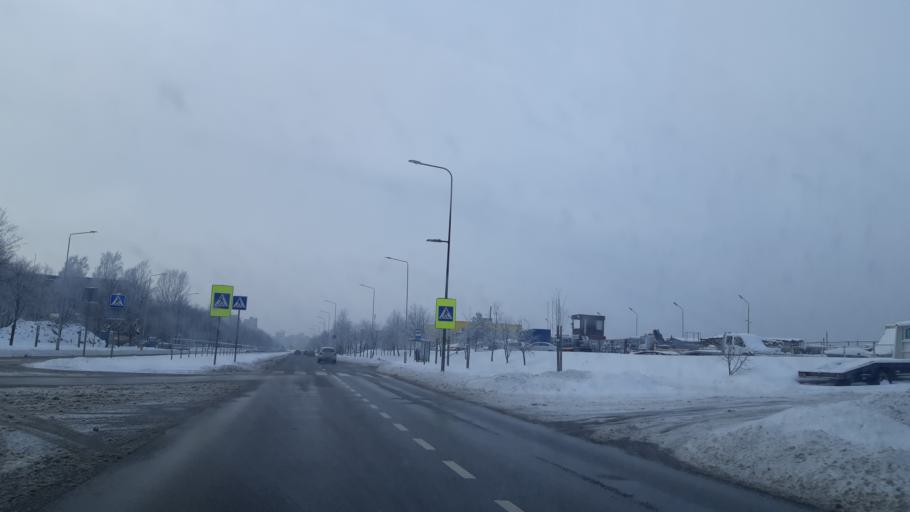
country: LT
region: Kauno apskritis
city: Dainava (Kaunas)
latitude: 54.9311
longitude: 23.9562
